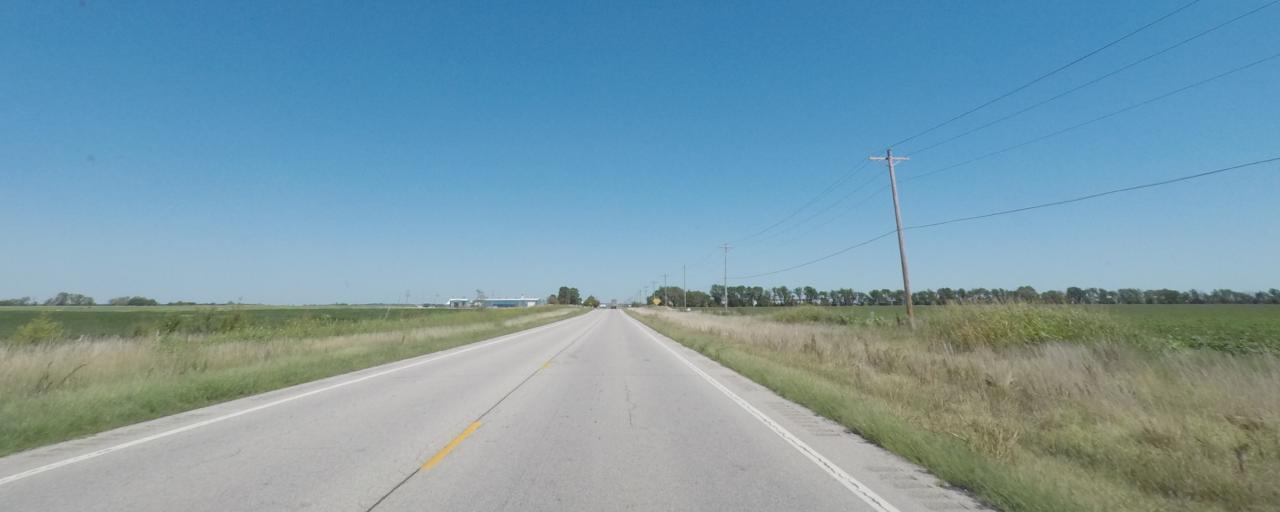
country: US
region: Kansas
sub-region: Sumner County
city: Wellington
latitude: 37.3150
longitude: -97.3847
